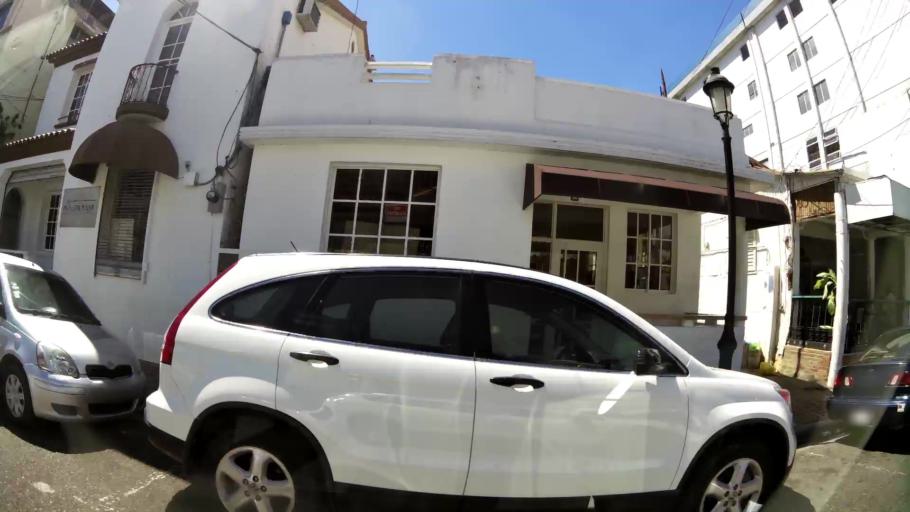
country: DO
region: Santiago
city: Santiago de los Caballeros
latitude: 19.4516
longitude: -70.6999
